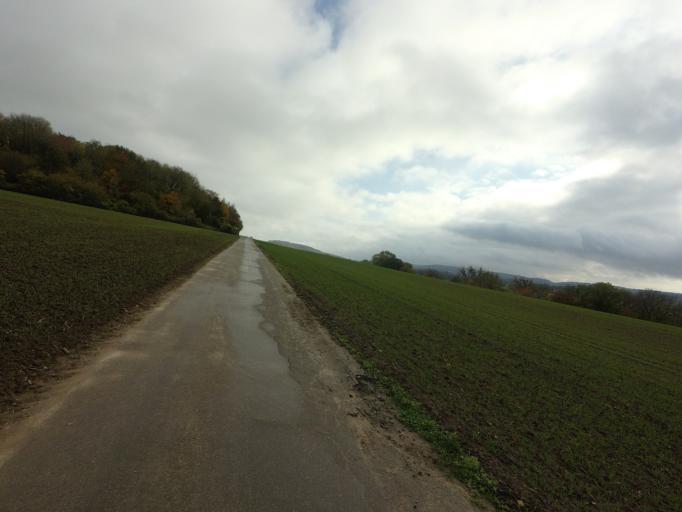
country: NL
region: Limburg
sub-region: Gemeente Simpelveld
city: Simpelveld
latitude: 50.7967
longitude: 5.9837
